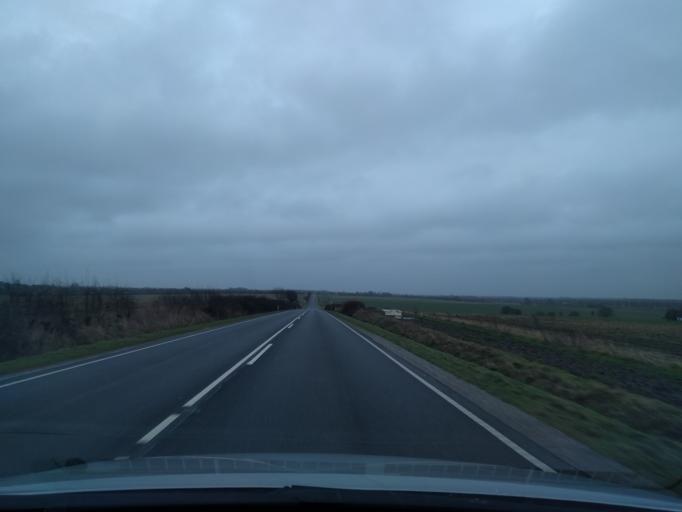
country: DK
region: South Denmark
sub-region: Tonder Kommune
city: Toftlund
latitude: 55.2492
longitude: 9.1765
